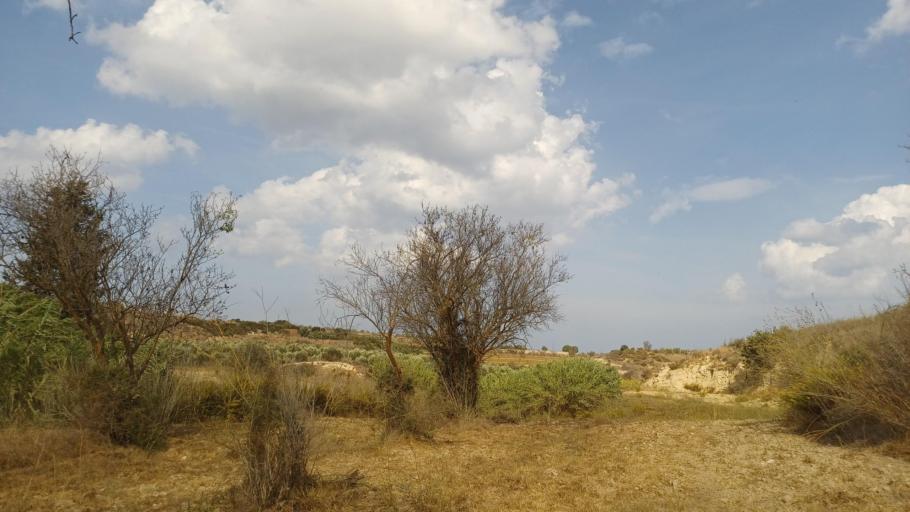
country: CY
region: Pafos
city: Polis
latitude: 35.0131
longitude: 32.4155
